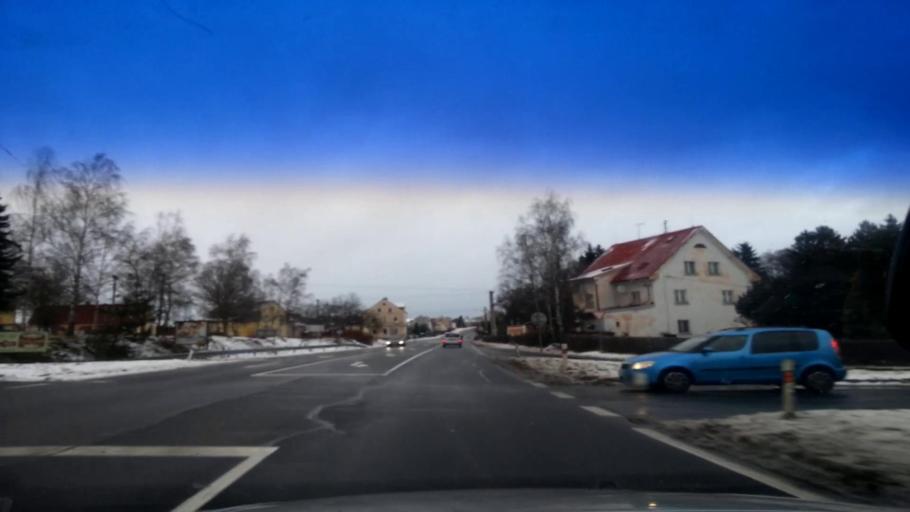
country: CZ
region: Karlovarsky
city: Hazlov
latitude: 50.1559
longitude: 12.2727
